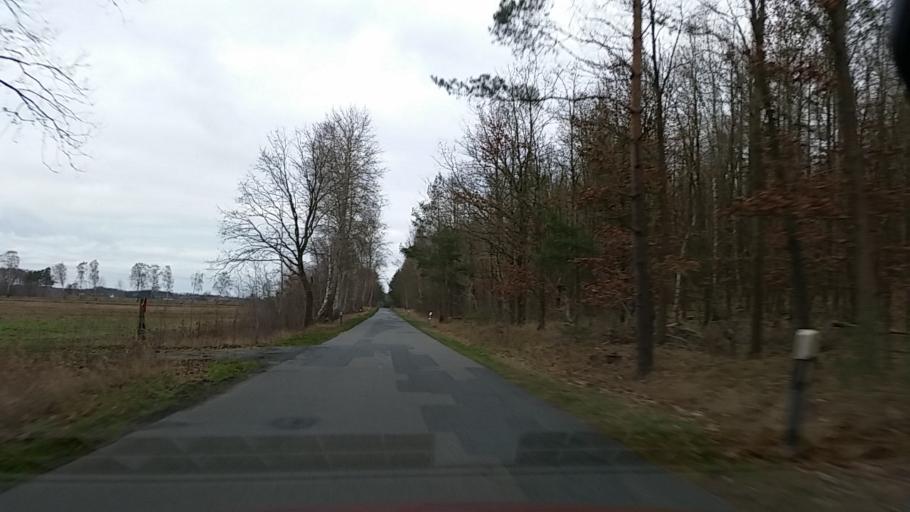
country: DE
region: Lower Saxony
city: Luder
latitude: 52.7889
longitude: 10.6697
